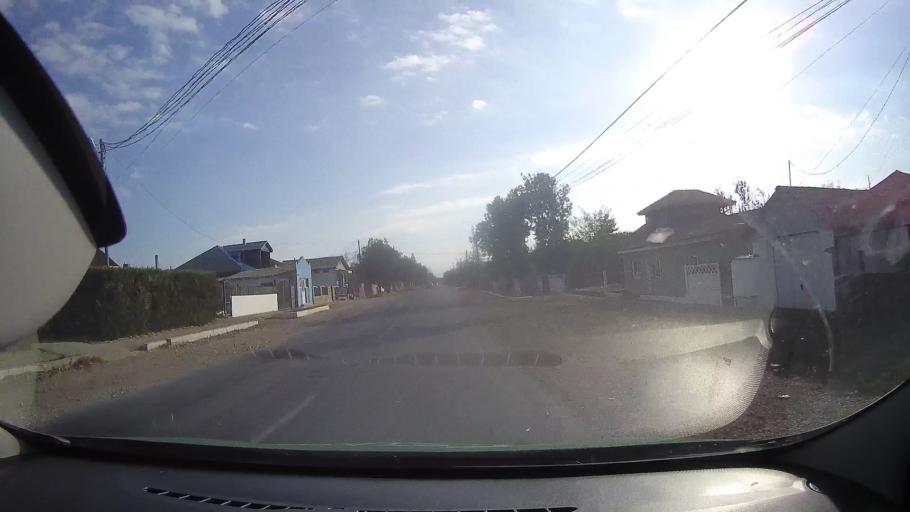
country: RO
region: Constanta
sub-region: Comuna Corbu
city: Corbu
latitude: 44.3871
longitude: 28.6622
